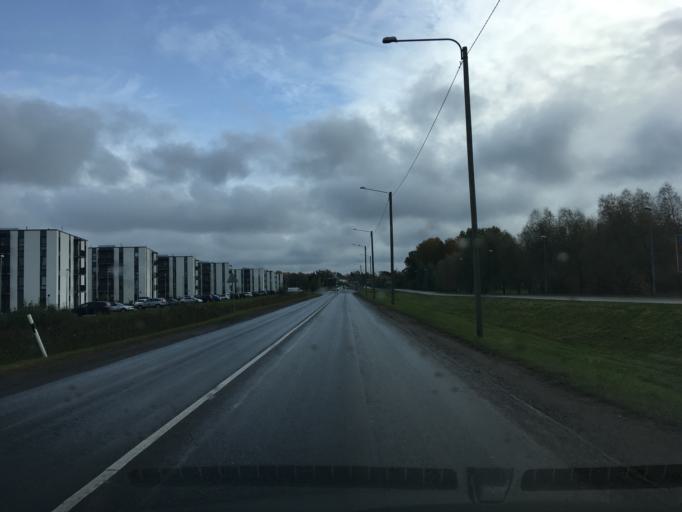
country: EE
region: Harju
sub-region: Saue vald
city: Laagri
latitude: 59.4297
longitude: 24.6146
